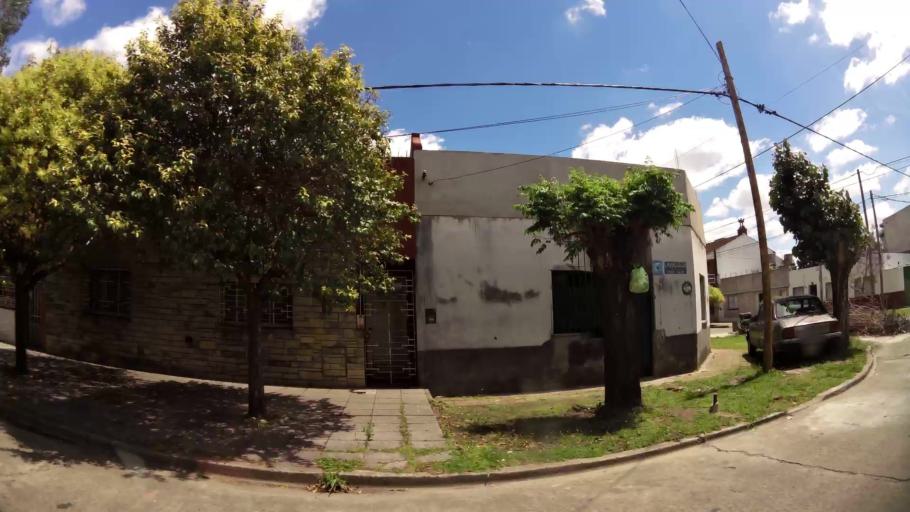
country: AR
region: Buenos Aires
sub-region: Partido de Lanus
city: Lanus
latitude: -34.7098
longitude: -58.4116
